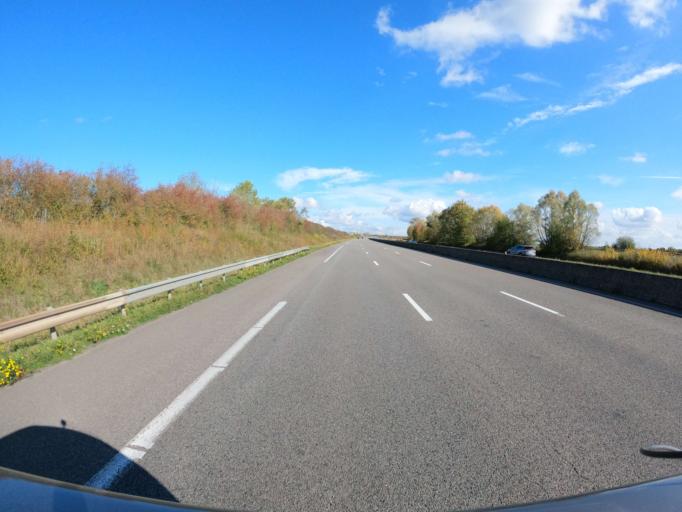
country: FR
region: Ile-de-France
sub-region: Departement des Yvelines
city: Sonchamp
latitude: 48.5371
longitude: 1.8770
